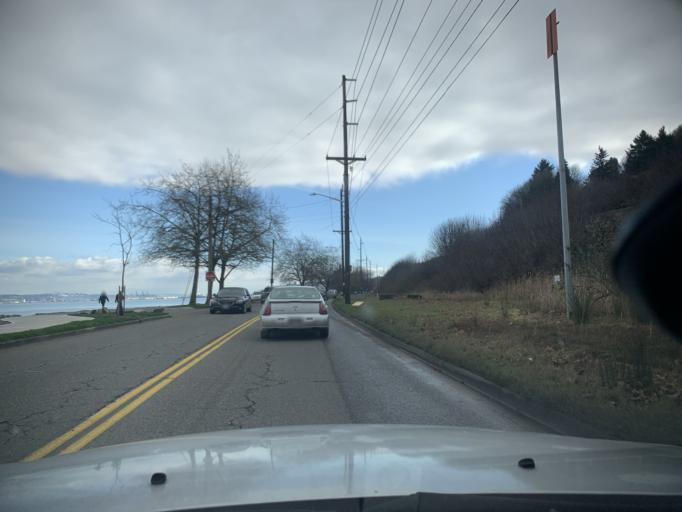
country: US
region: Washington
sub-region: Pierce County
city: Fircrest
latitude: 47.2929
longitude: -122.4961
